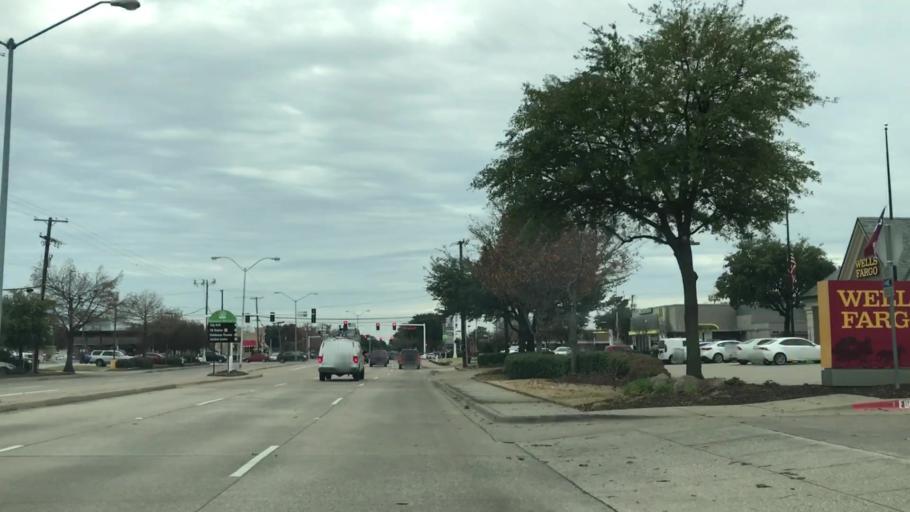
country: US
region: Texas
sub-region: Dallas County
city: Farmers Branch
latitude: 32.9257
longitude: -96.8817
